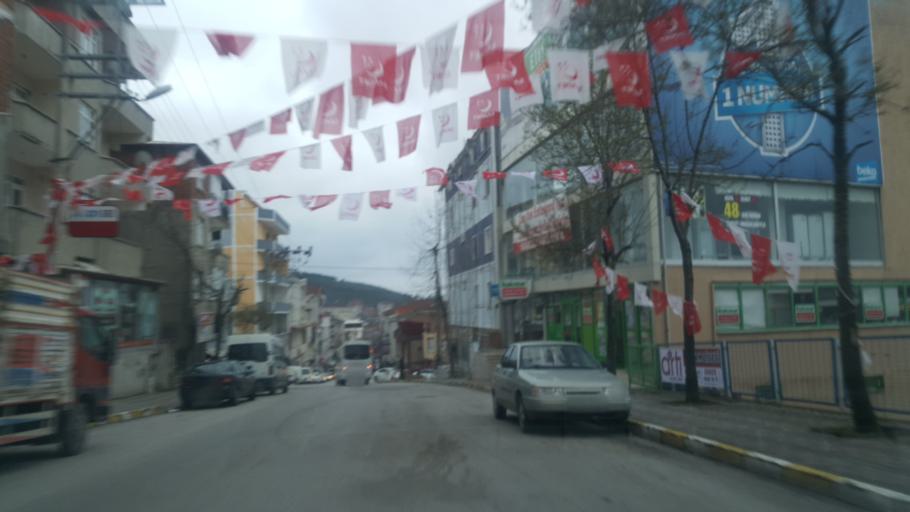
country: TR
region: Kocaeli
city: Tavsancil
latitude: 40.7871
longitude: 29.5394
